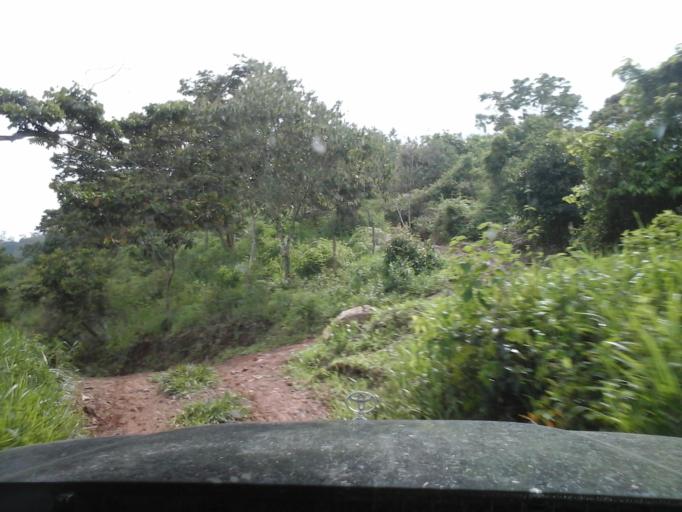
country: CO
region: Cesar
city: Agustin Codazzi
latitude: 9.9543
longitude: -73.0640
